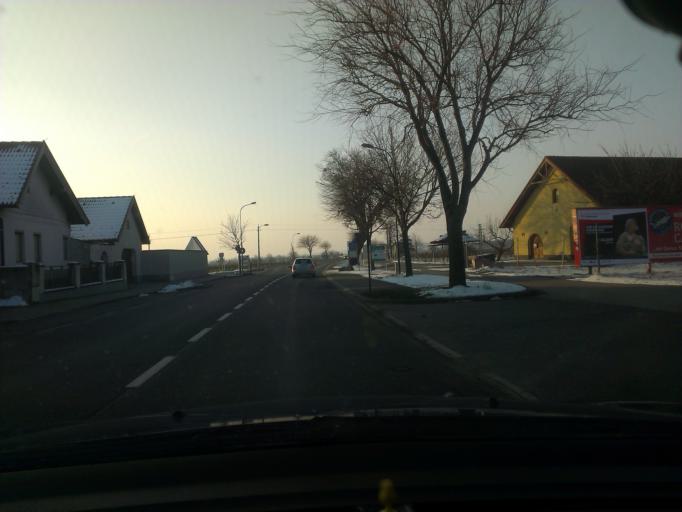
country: AT
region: Burgenland
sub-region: Eisenstadt-Umgebung
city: Donnerskirchen
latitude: 47.8919
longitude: 16.6477
